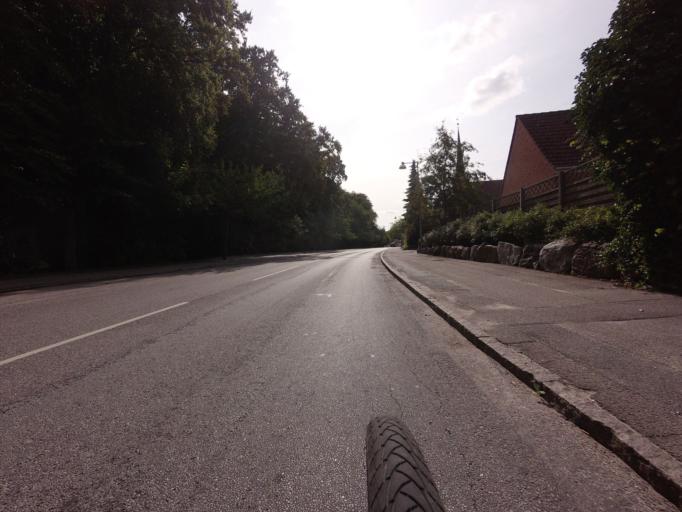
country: DK
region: Zealand
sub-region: Faxe Kommune
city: Fakse Ladeplads
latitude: 55.2172
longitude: 12.1661
